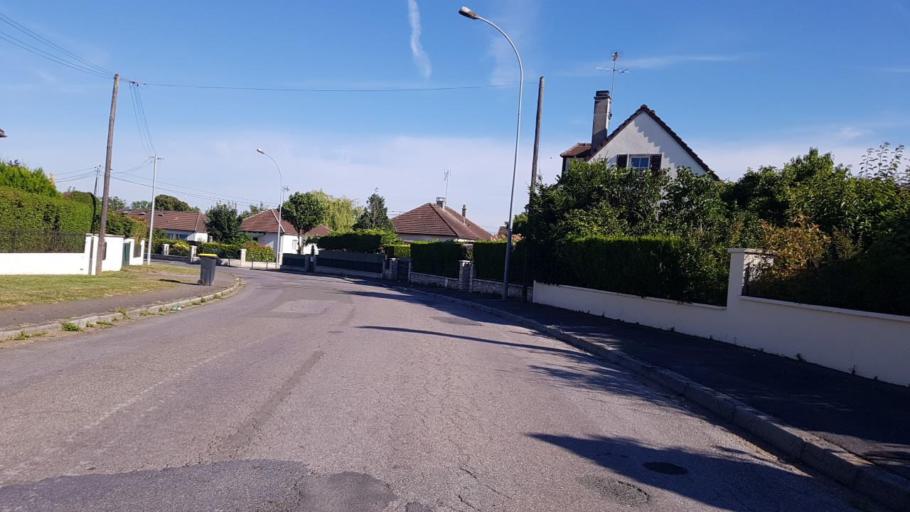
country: FR
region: Picardie
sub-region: Departement de l'Oise
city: Chamant
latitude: 49.2098
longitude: 2.5989
